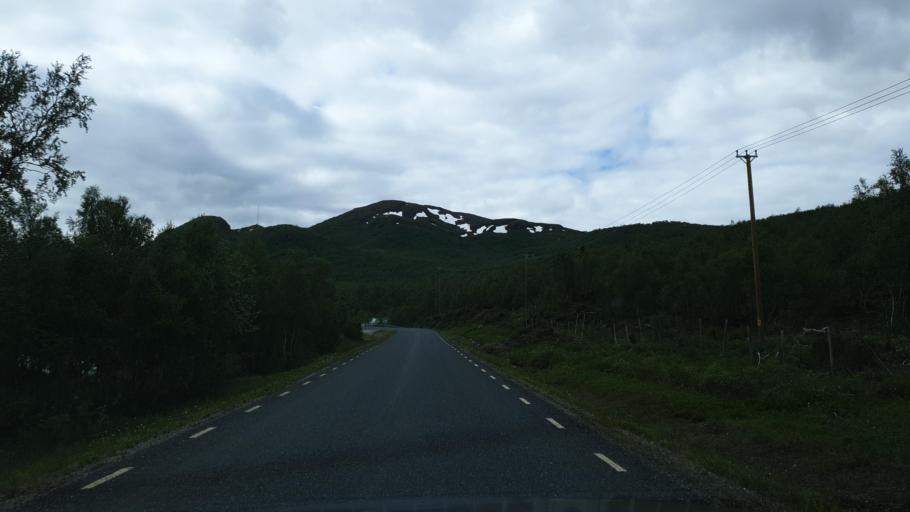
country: NO
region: Nordland
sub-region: Hattfjelldal
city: Hattfjelldal
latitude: 65.4251
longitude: 14.6545
